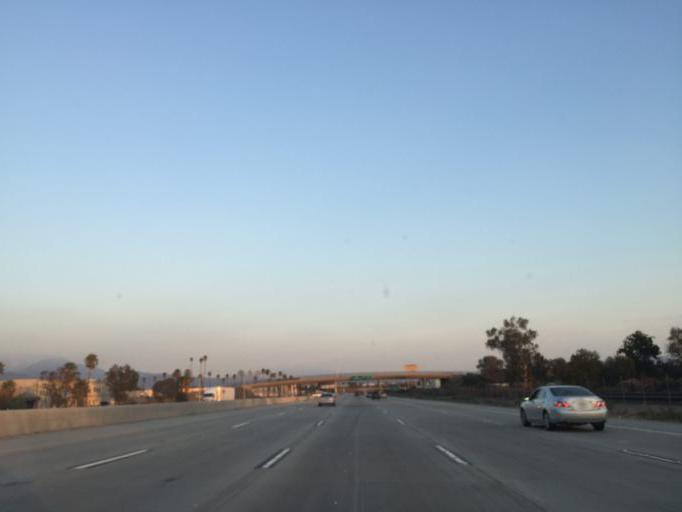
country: US
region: California
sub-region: San Bernardino County
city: San Bernardino
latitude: 34.1351
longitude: -117.3117
